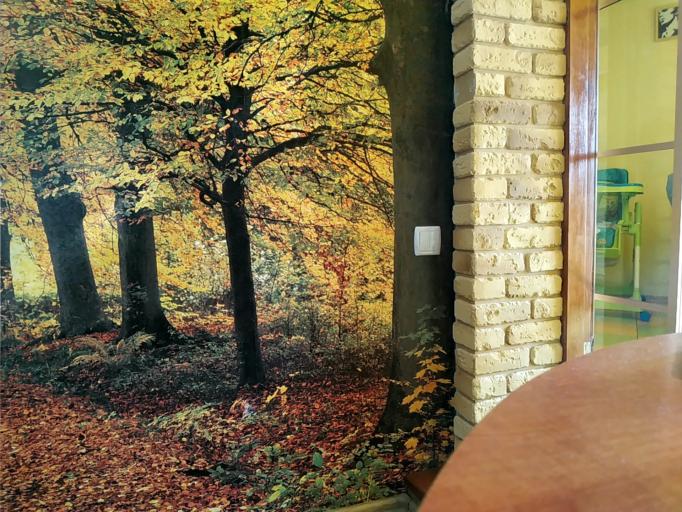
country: RU
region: Novgorod
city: Parfino
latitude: 57.8061
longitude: 31.5898
